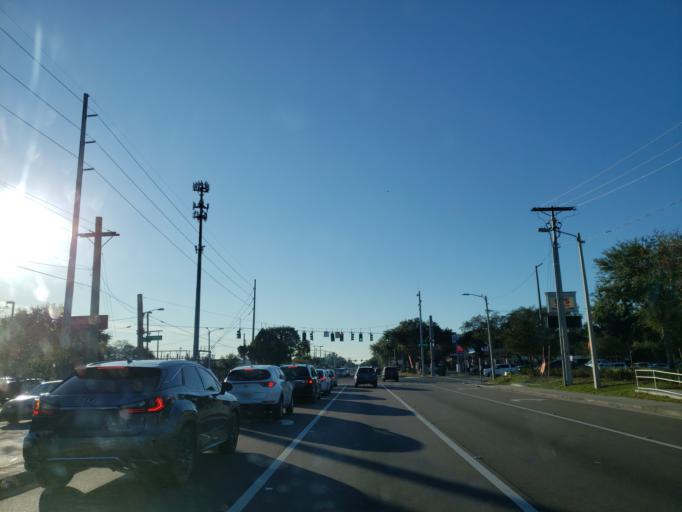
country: US
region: Florida
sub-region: Hillsborough County
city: Bloomingdale
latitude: 27.8937
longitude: -82.2685
